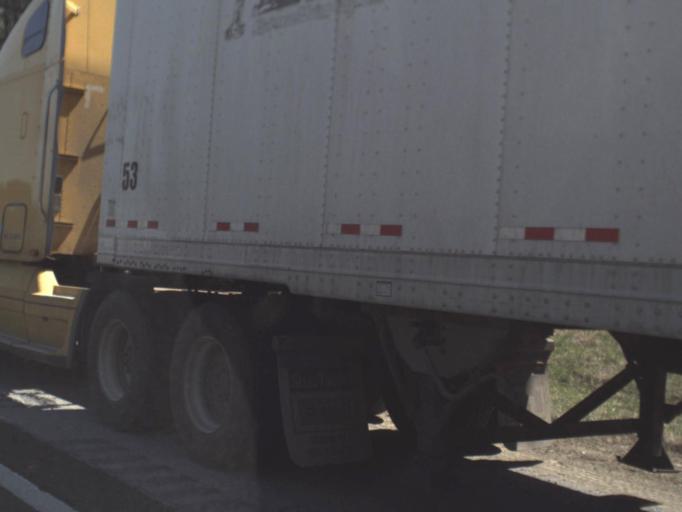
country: US
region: Florida
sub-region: Holmes County
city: Bonifay
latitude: 30.7565
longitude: -85.6297
